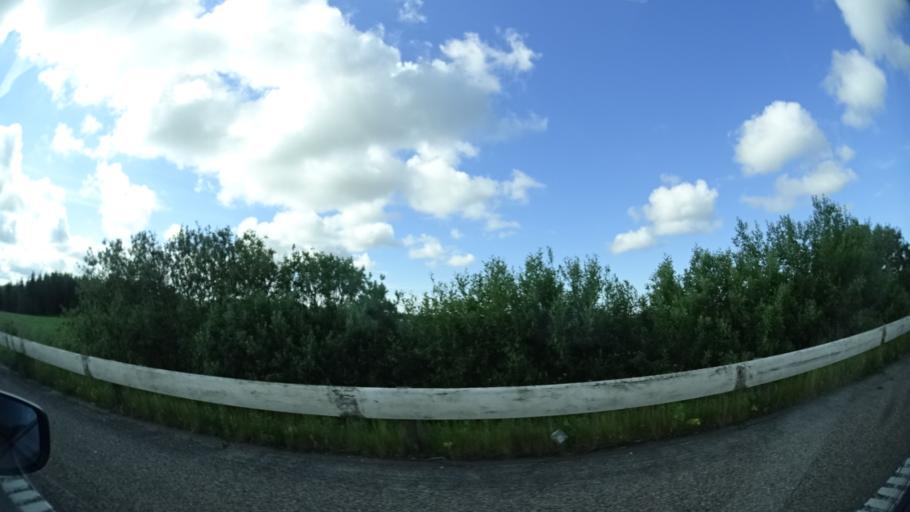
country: DK
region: Central Jutland
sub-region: Syddjurs Kommune
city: Ronde
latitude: 56.3179
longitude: 10.4713
